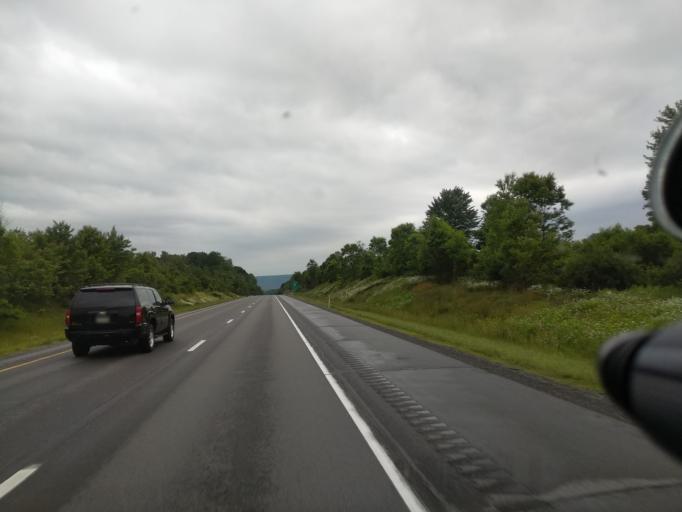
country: US
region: Pennsylvania
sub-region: Clinton County
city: Avis
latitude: 41.0545
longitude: -77.2836
